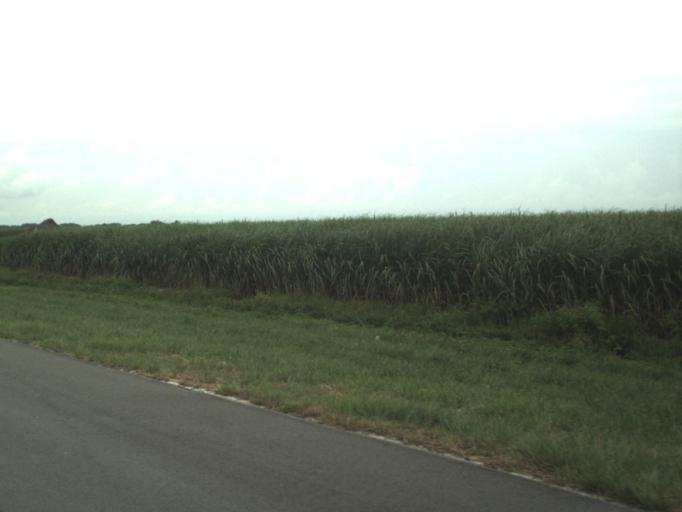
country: US
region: Florida
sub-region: Palm Beach County
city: Belle Glade
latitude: 26.7264
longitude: -80.6503
